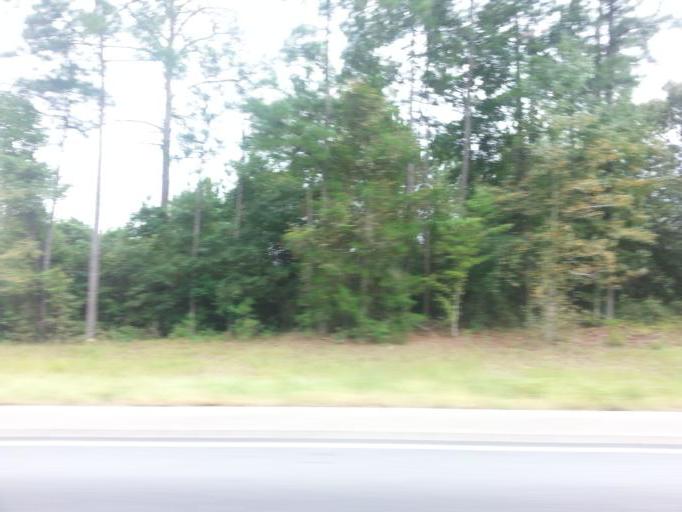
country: US
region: Alabama
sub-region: Escambia County
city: Brewton
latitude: 31.3143
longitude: -87.1515
